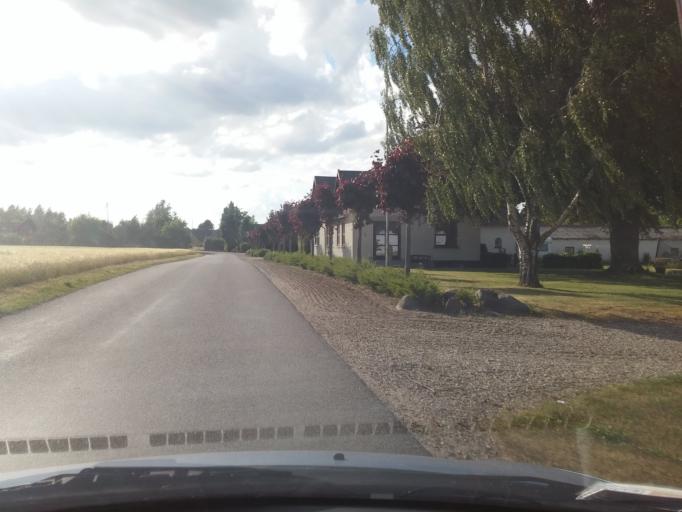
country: DK
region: South Denmark
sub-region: Kerteminde Kommune
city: Langeskov
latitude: 55.3926
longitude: 10.5656
